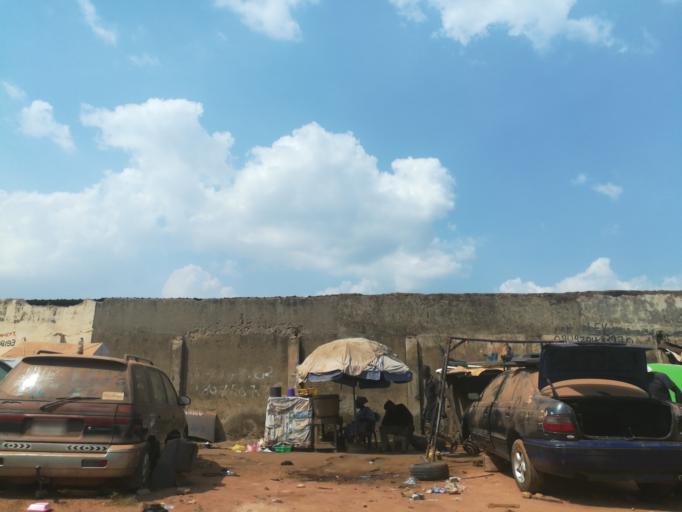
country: NG
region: Abuja Federal Capital Territory
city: Abuja
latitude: 9.0628
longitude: 7.4340
